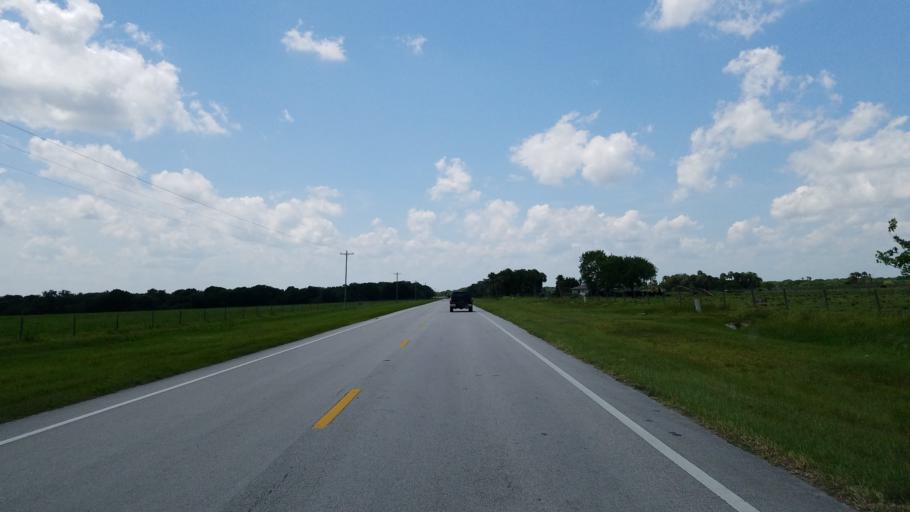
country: US
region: Florida
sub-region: Okeechobee County
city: Okeechobee
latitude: 27.3069
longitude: -80.9014
